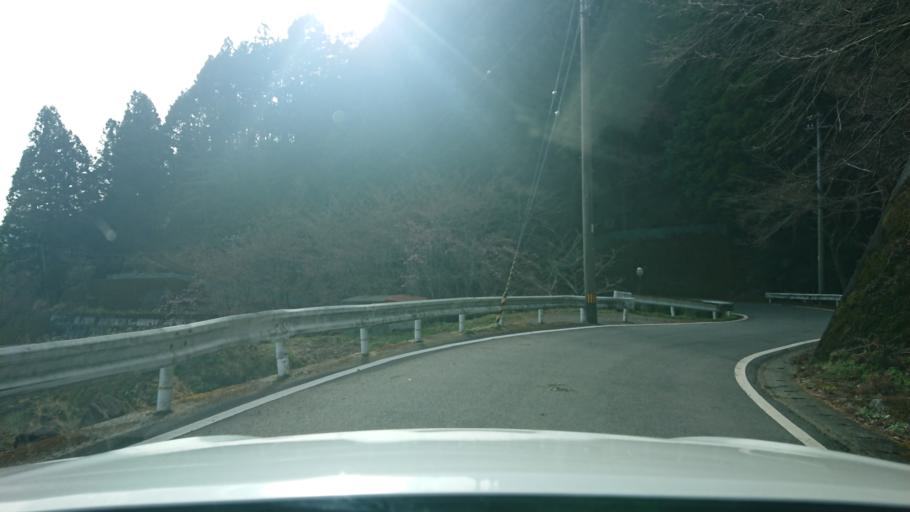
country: JP
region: Tokushima
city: Ishii
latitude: 33.9148
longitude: 134.4092
